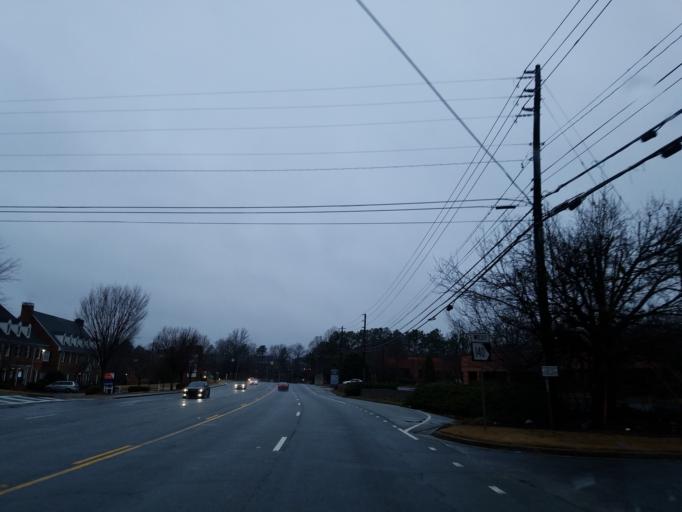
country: US
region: Georgia
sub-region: Gwinnett County
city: Norcross
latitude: 33.9632
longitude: -84.2506
